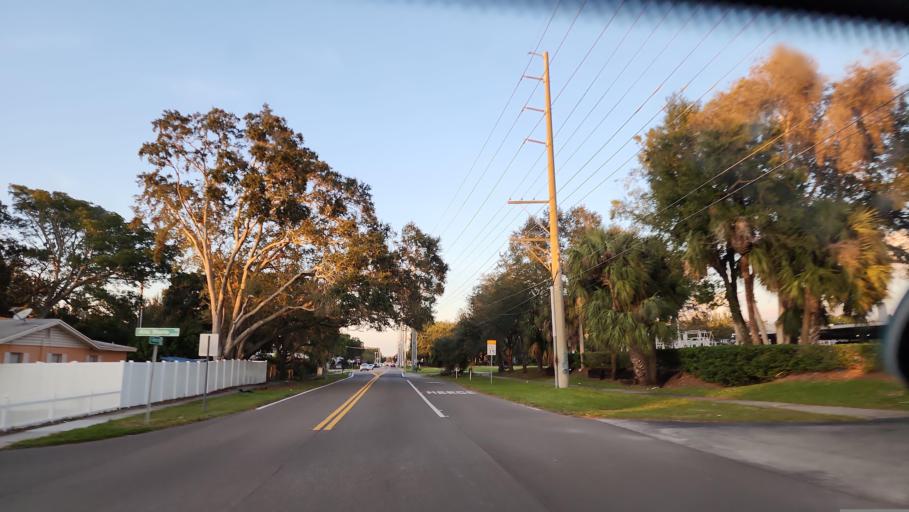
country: US
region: Florida
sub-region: Hillsborough County
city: Town 'n' Country
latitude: 27.9920
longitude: -82.5504
